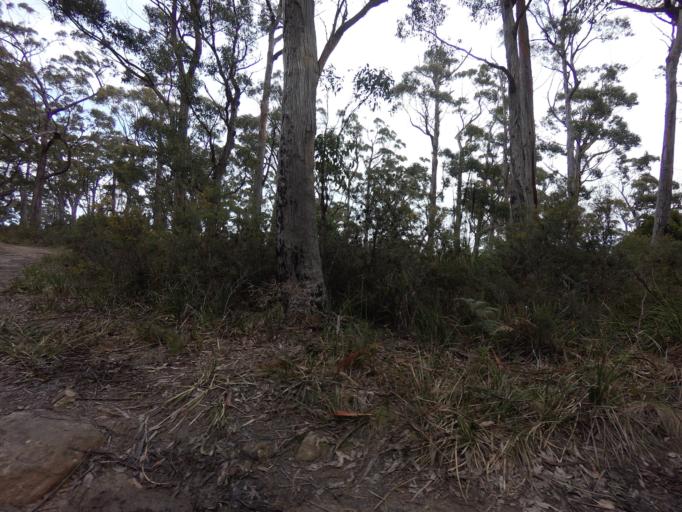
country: AU
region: Tasmania
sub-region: Huon Valley
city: Geeveston
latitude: -43.4759
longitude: 146.9341
